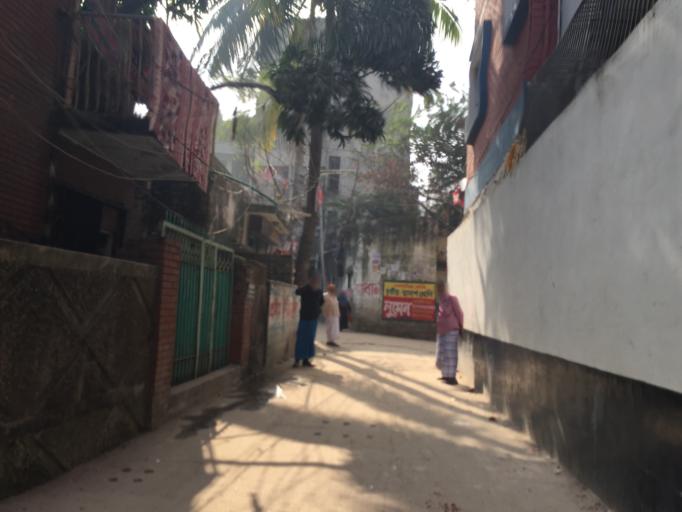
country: BD
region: Dhaka
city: Azimpur
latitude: 23.7903
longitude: 90.3610
